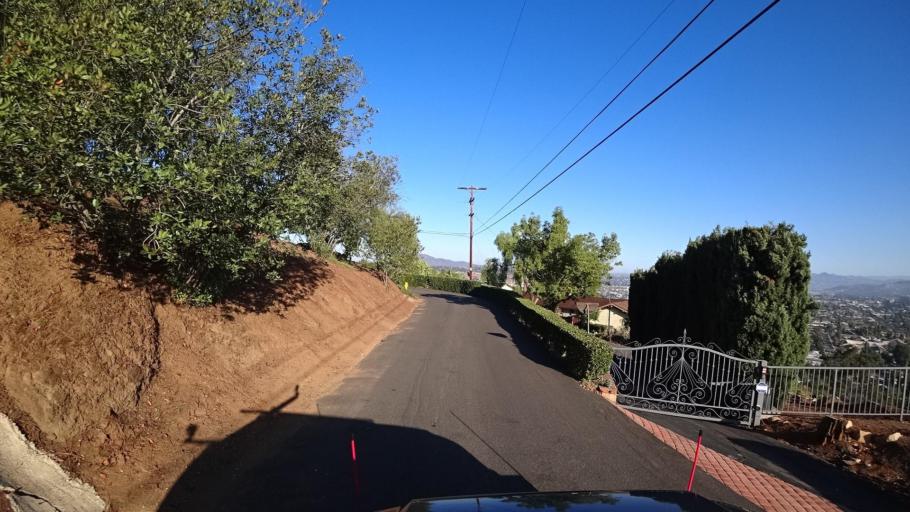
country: US
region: California
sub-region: San Diego County
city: Casa de Oro-Mount Helix
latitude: 32.7726
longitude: -116.9644
